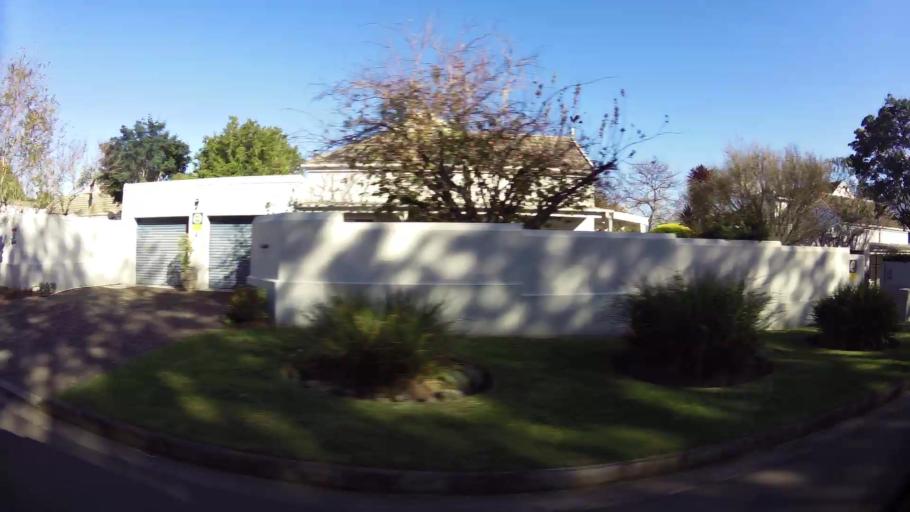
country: ZA
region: Western Cape
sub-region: Eden District Municipality
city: George
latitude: -33.9543
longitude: 22.4237
